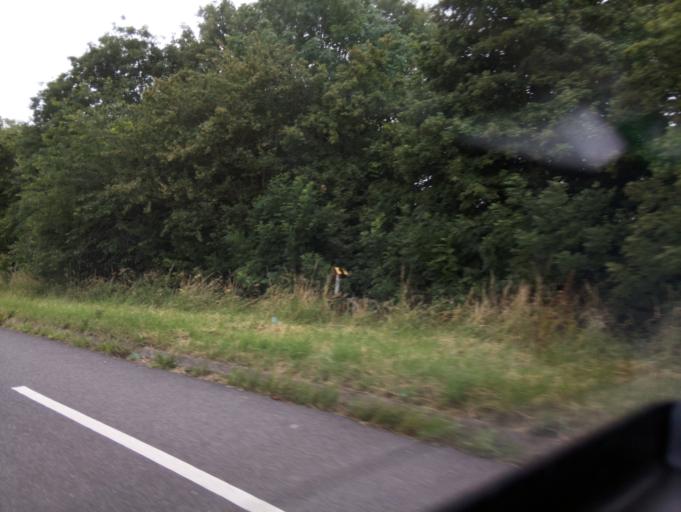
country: GB
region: England
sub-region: Gloucestershire
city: Tewkesbury
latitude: 51.9656
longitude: -2.1583
